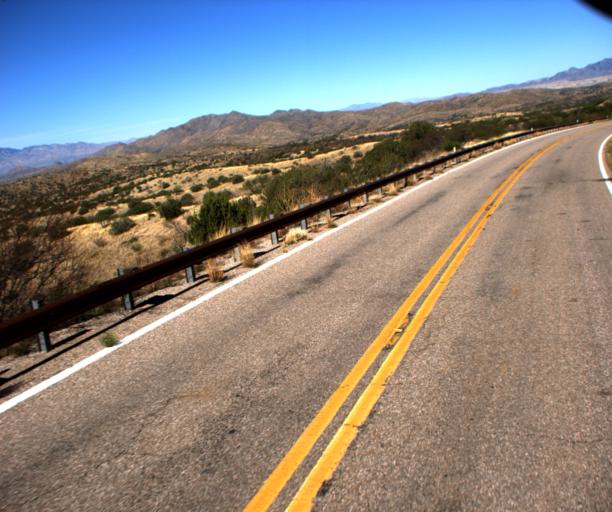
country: US
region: Arizona
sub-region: Pima County
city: Corona de Tucson
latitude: 31.8312
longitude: -110.7107
